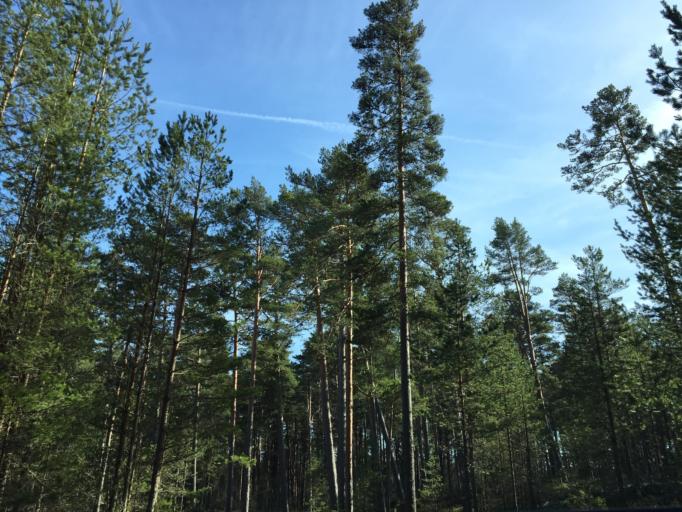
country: EE
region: Paernumaa
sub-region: Paernu linn
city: Parnu
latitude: 58.2308
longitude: 24.5182
